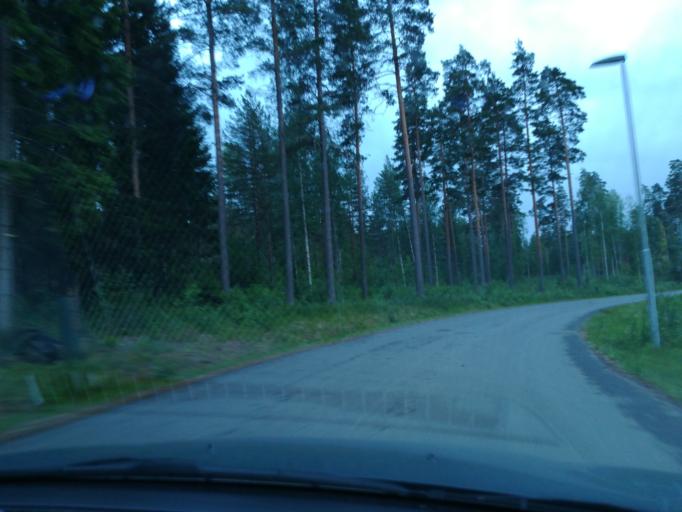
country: FI
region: Southern Savonia
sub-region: Mikkeli
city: Ristiina
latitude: 61.4921
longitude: 27.2743
